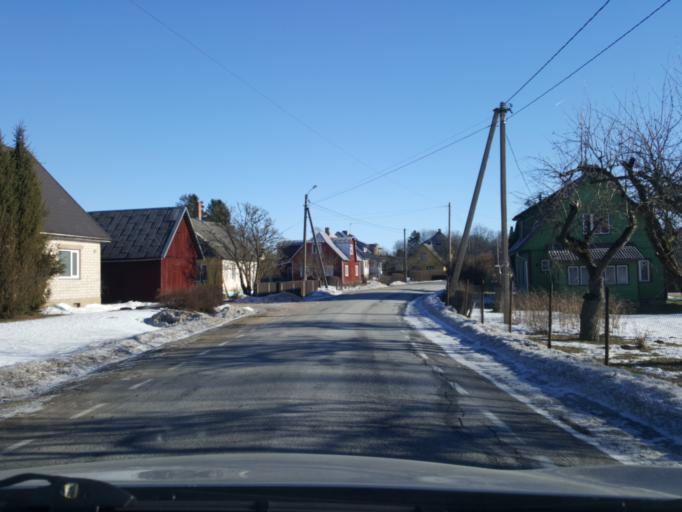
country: EE
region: Viljandimaa
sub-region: Suure-Jaani vald
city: Suure-Jaani
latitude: 58.5460
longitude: 25.5414
